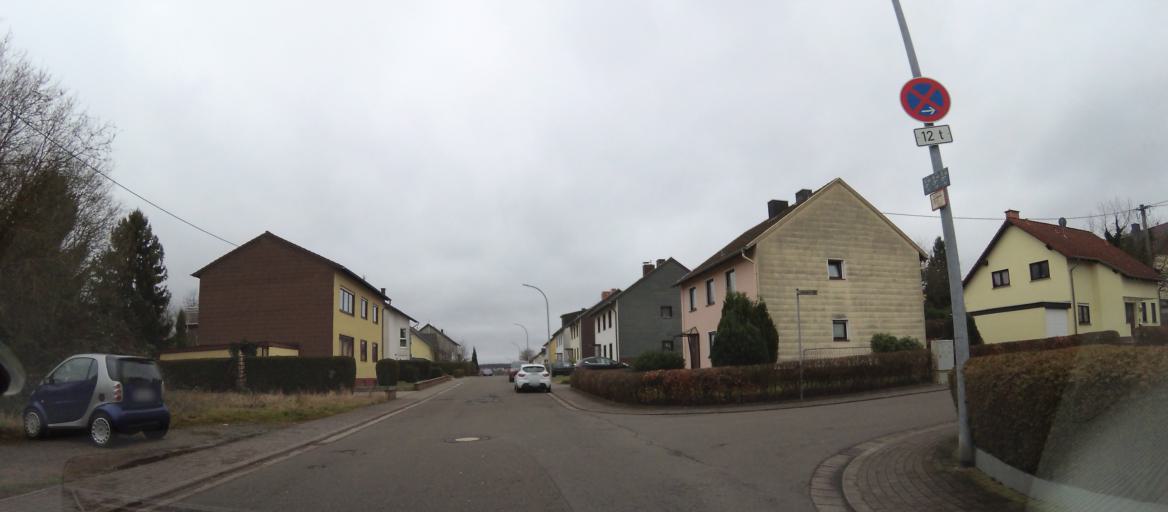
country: DE
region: Saarland
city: Schiffweiler
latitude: 49.3596
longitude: 7.1160
